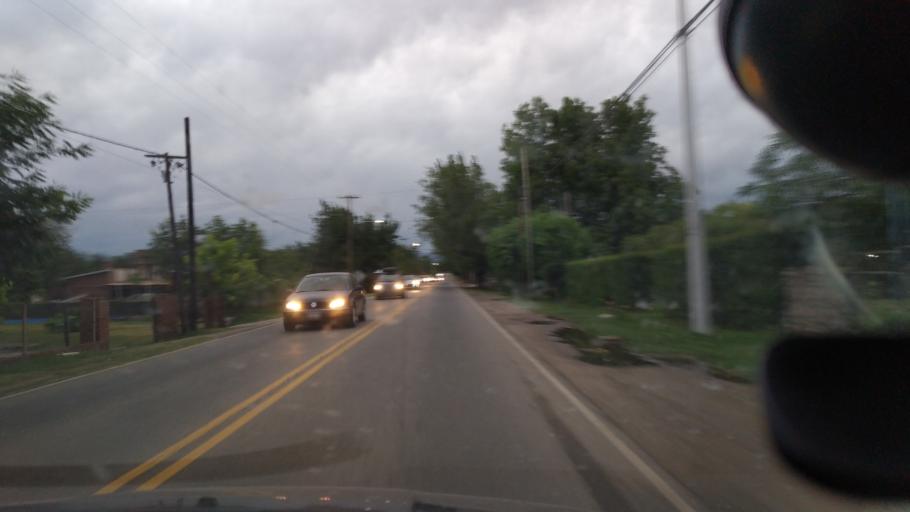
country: AR
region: Cordoba
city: Villa Las Rosas
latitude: -31.9172
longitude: -65.0377
